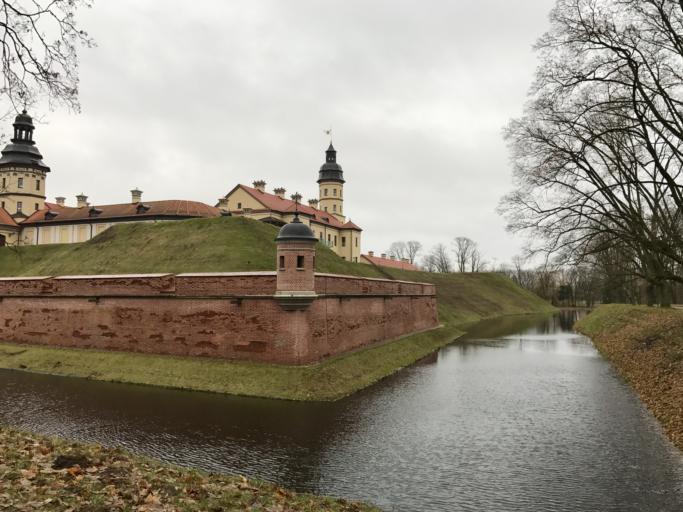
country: BY
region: Minsk
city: Nyasvizh
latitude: 53.2228
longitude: 26.6896
